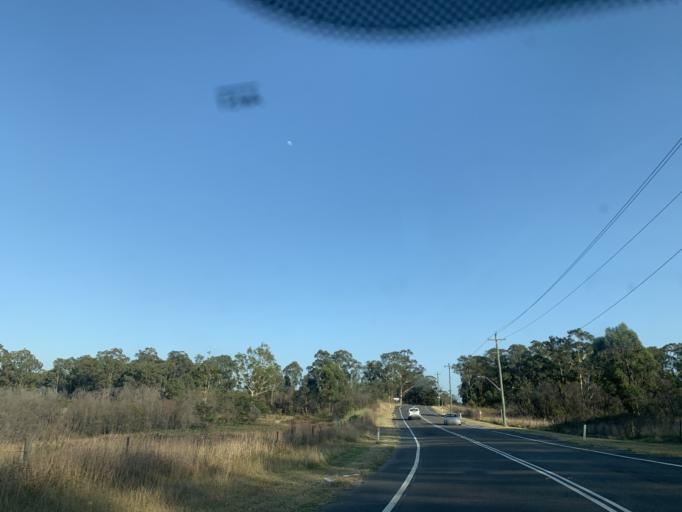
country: AU
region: New South Wales
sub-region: Fairfield
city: Horsley Park
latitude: -33.8314
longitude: 150.8738
